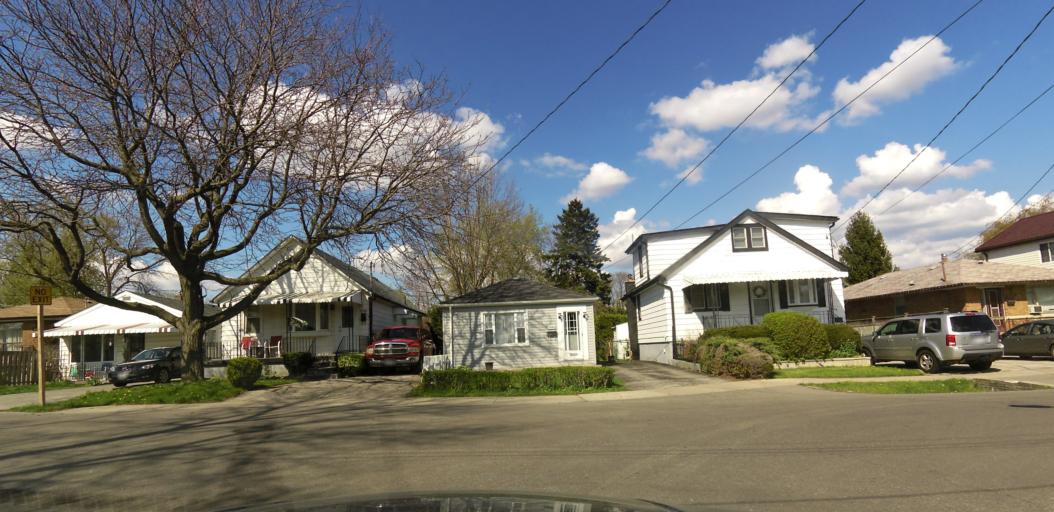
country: CA
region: Ontario
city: Etobicoke
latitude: 43.5773
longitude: -79.5625
